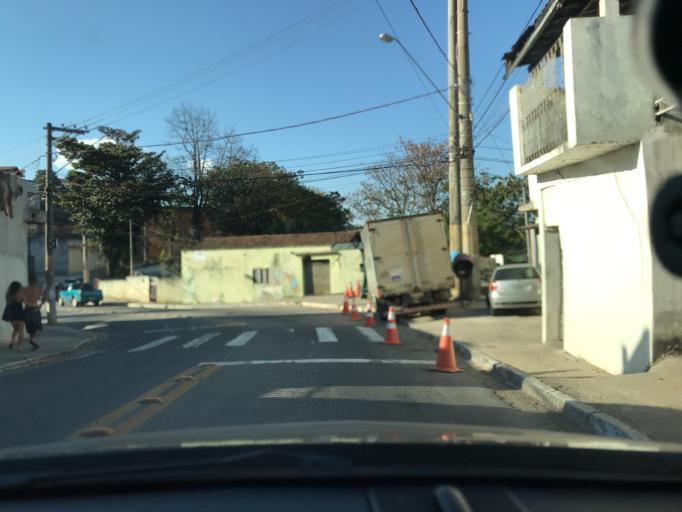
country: BR
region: Sao Paulo
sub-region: Sao Jose Dos Campos
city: Sao Jose dos Campos
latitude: -23.1567
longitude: -45.9024
